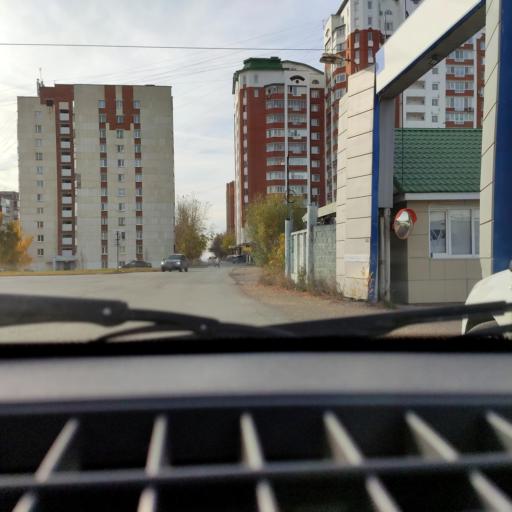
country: RU
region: Bashkortostan
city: Ufa
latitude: 54.7047
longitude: 55.9923
